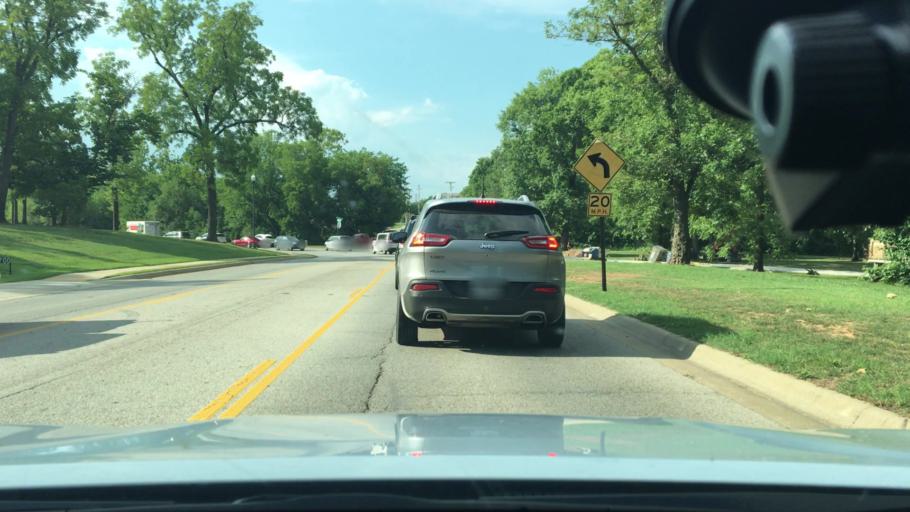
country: US
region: Arkansas
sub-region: Benton County
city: Bentonville
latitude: 36.3323
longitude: -94.1886
